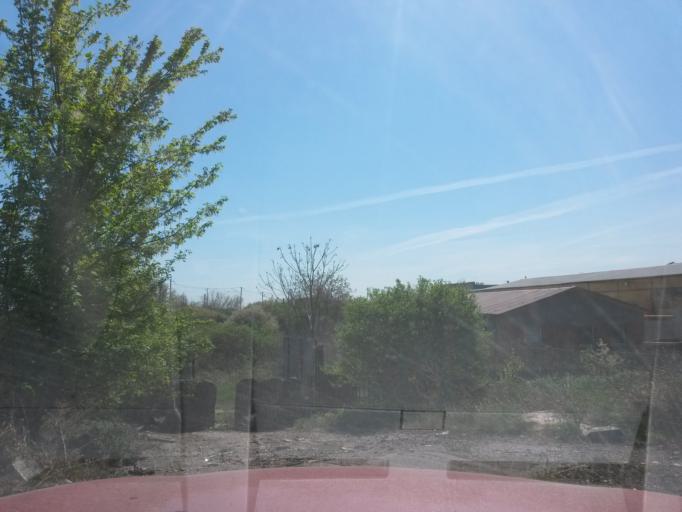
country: SK
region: Kosicky
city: Kosice
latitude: 48.6731
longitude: 21.2773
